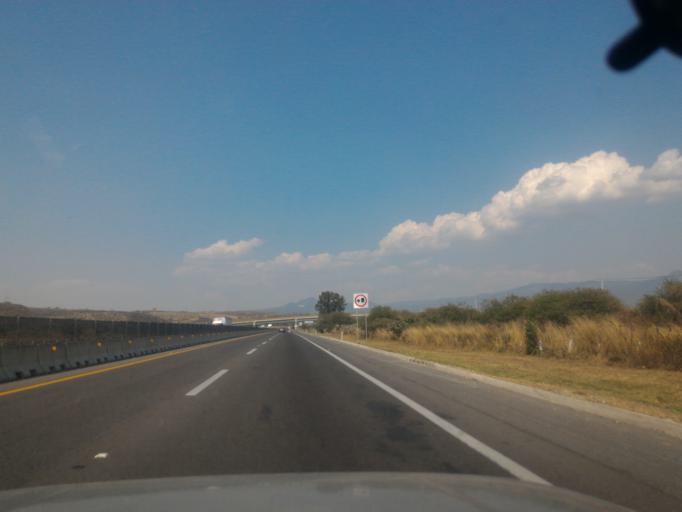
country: MX
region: Jalisco
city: Gomez Farias
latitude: 19.7699
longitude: -103.5158
